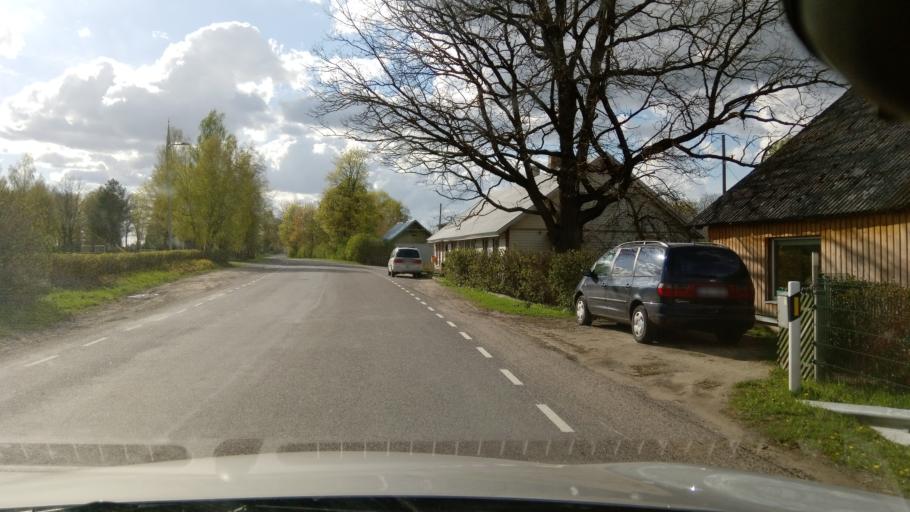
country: EE
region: Jaervamaa
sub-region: Jaerva-Jaani vald
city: Jarva-Jaani
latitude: 58.9422
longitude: 25.8422
